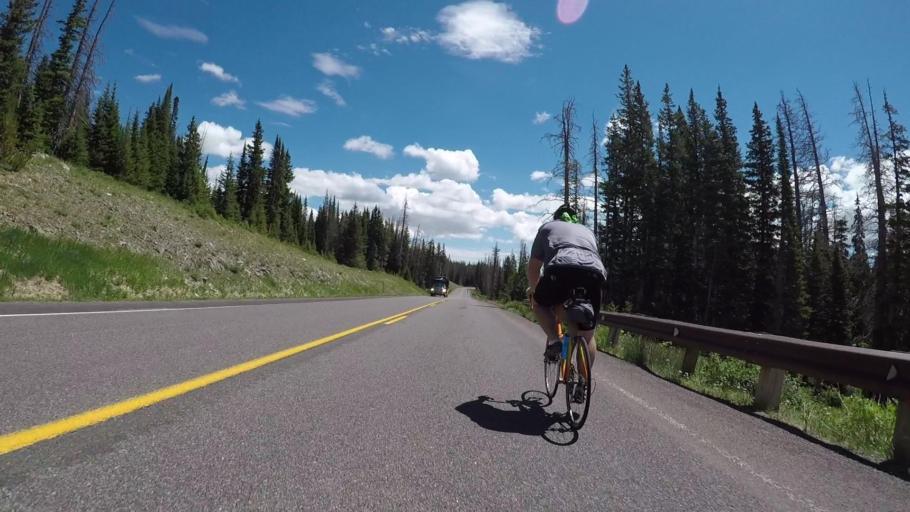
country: US
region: Wyoming
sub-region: Carbon County
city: Saratoga
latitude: 41.3517
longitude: -106.2697
